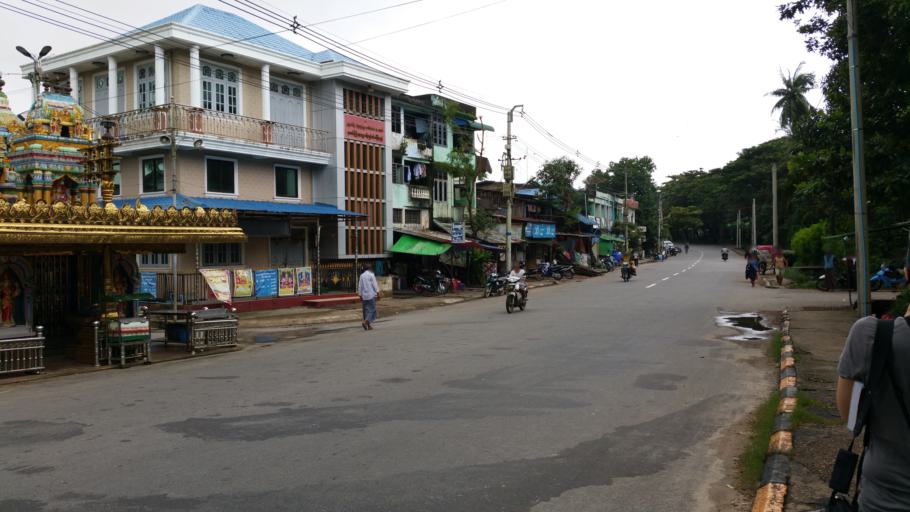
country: MM
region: Mon
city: Mawlamyine
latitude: 16.4872
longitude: 97.6244
